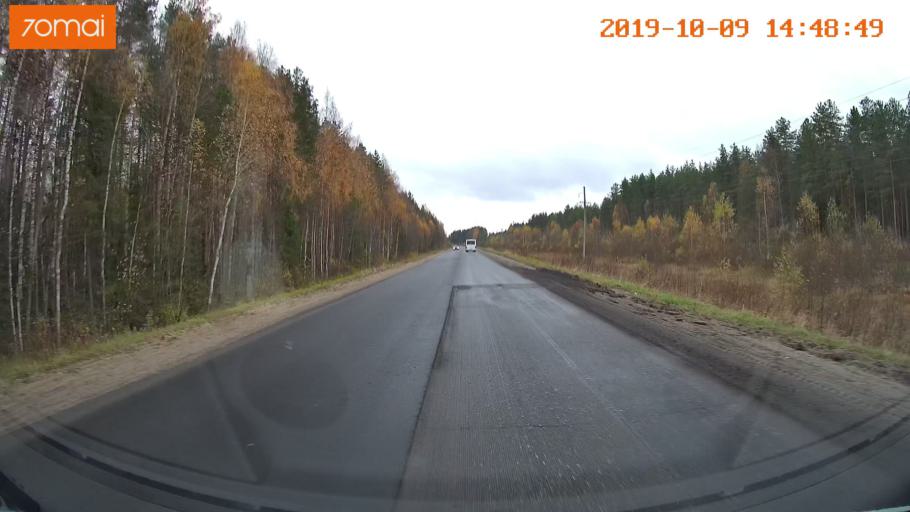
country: RU
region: Kostroma
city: Chistyye Bory
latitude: 58.4009
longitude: 41.5772
